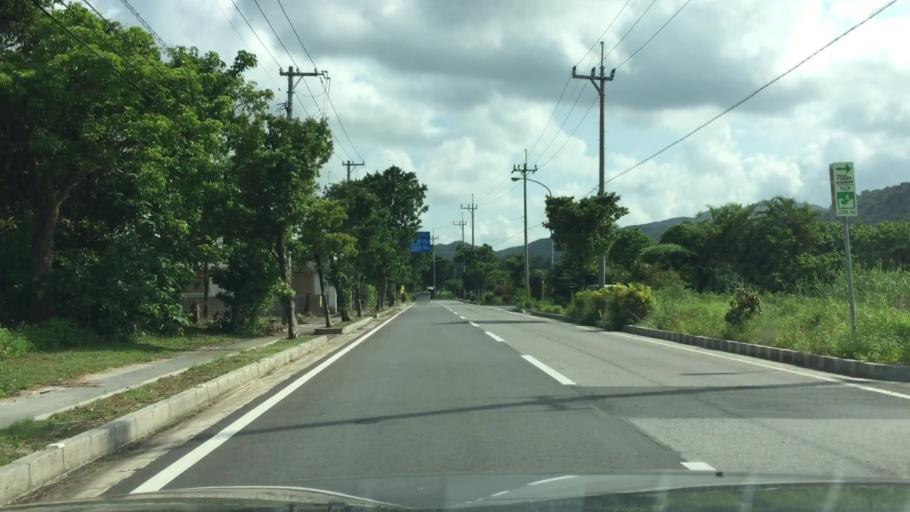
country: JP
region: Okinawa
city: Ishigaki
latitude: 24.4674
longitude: 124.2506
